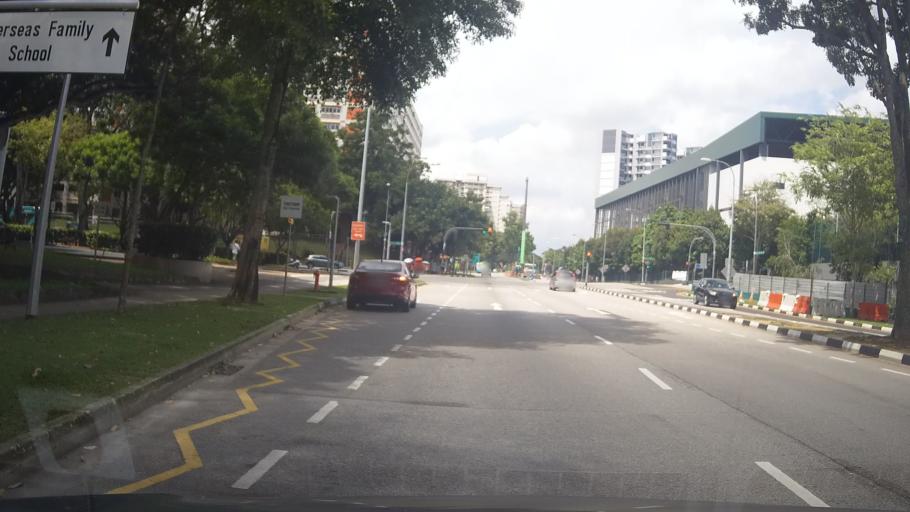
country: MY
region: Johor
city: Kampung Pasir Gudang Baru
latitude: 1.3790
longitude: 103.9424
